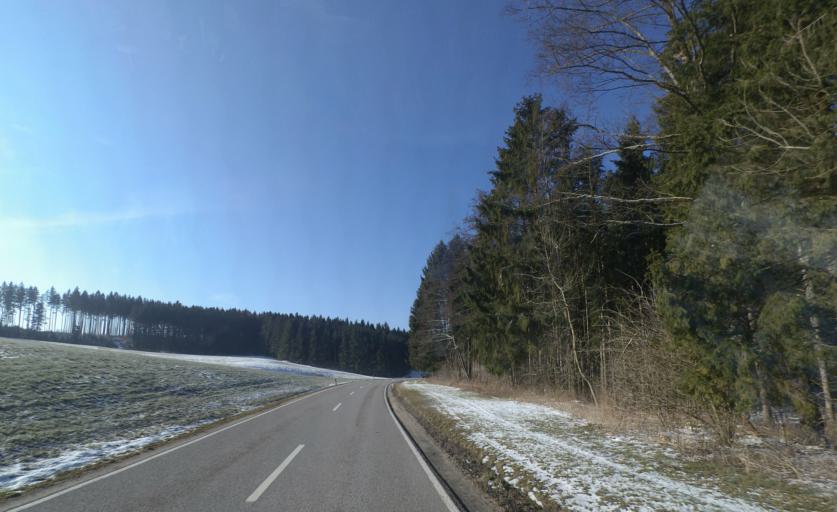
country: DE
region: Bavaria
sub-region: Upper Bavaria
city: Chieming
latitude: 47.9408
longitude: 12.5423
